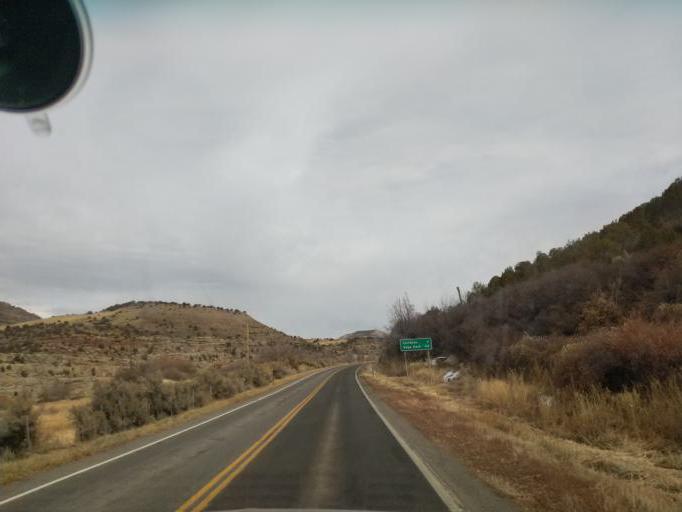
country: US
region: Colorado
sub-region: Mesa County
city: Palisade
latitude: 39.1874
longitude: -108.1341
